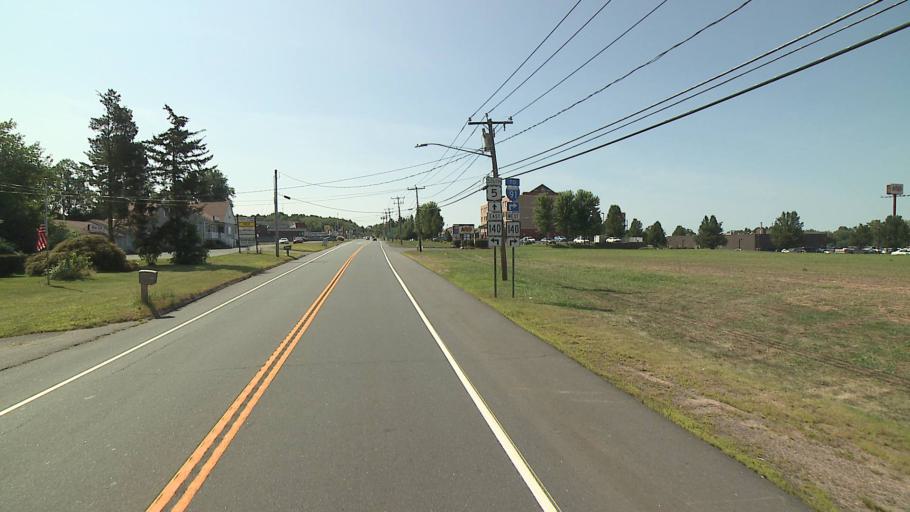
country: US
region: Connecticut
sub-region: Hartford County
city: Windsor Locks
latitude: 41.9330
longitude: -72.6046
